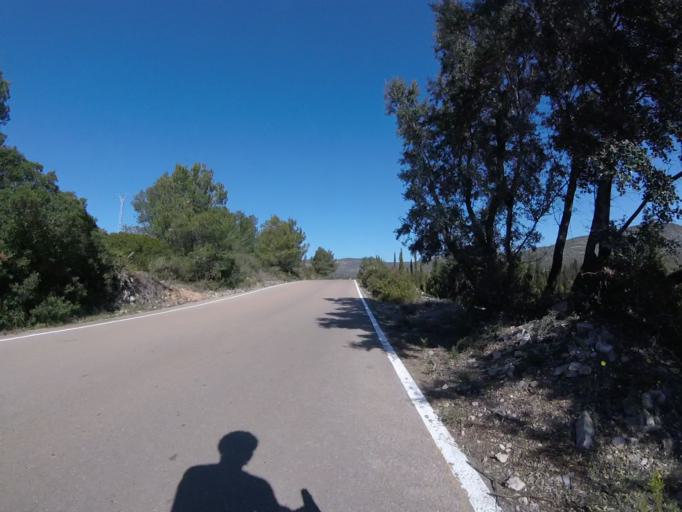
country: ES
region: Valencia
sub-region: Provincia de Castello
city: Santa Magdalena de Pulpis
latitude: 40.3677
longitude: 0.2753
